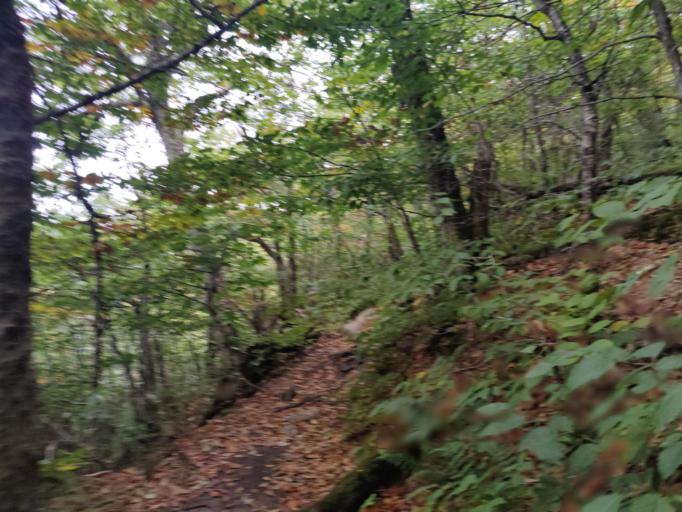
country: US
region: Vermont
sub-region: Bennington County
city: Manchester Center
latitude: 43.2671
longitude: -72.9417
